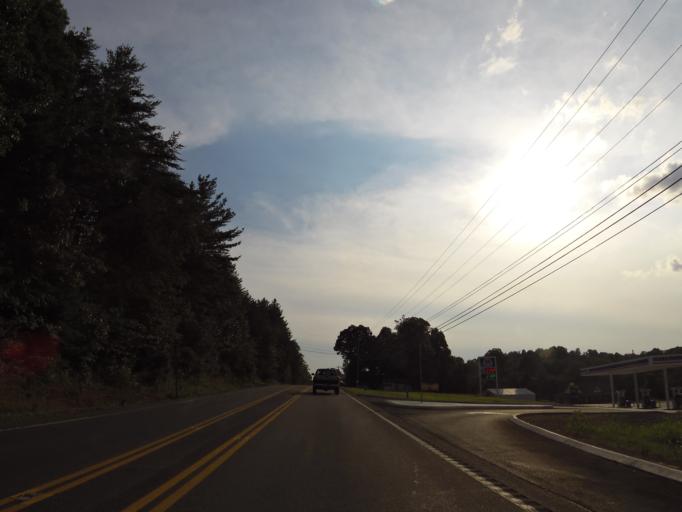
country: US
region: Tennessee
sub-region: Morgan County
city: Coalfield
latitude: 36.0377
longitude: -84.4024
